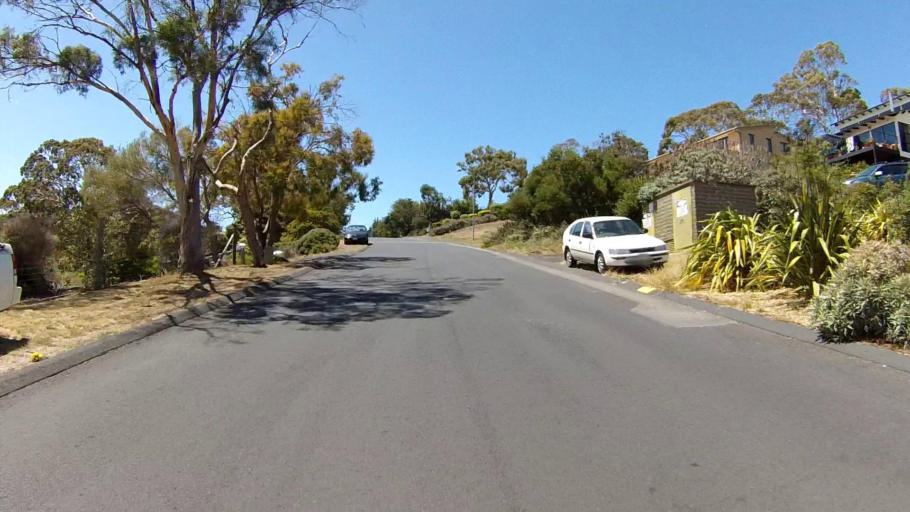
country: AU
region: Tasmania
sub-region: Clarence
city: Sandford
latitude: -42.9191
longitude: 147.5048
